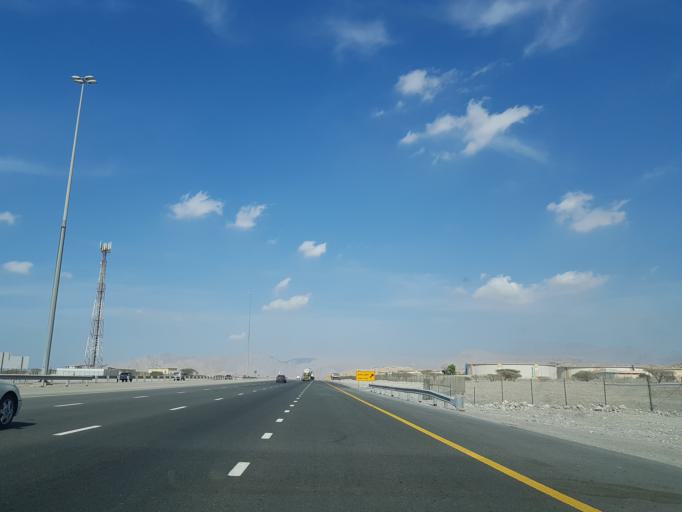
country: AE
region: Ra's al Khaymah
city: Ras al-Khaimah
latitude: 25.7687
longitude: 56.0260
